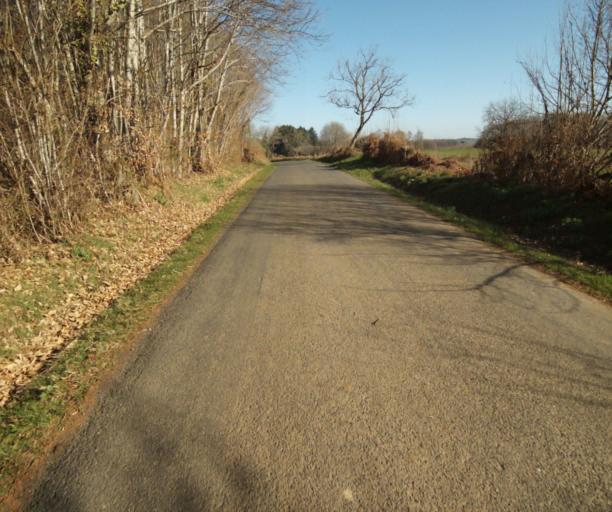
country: FR
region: Limousin
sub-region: Departement de la Correze
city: Saint-Clement
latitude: 45.3726
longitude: 1.6463
